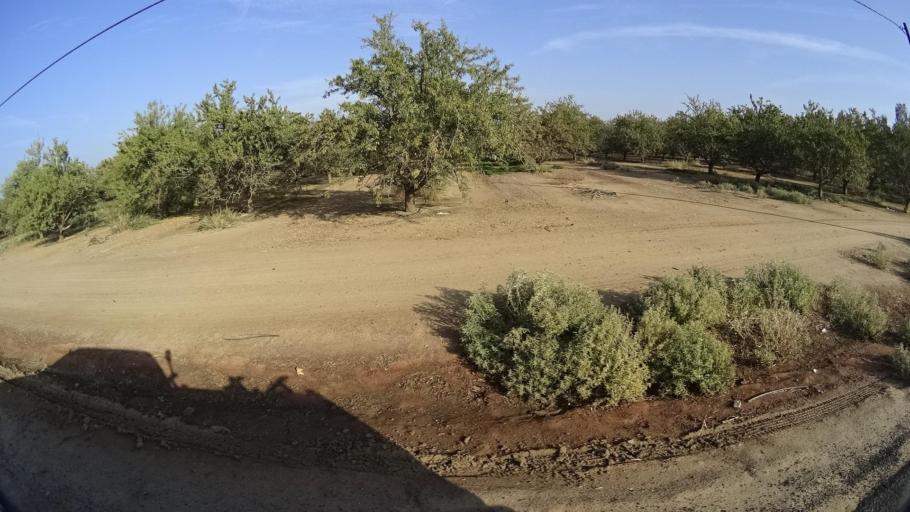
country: US
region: California
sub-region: Kern County
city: McFarland
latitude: 35.6745
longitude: -119.2164
